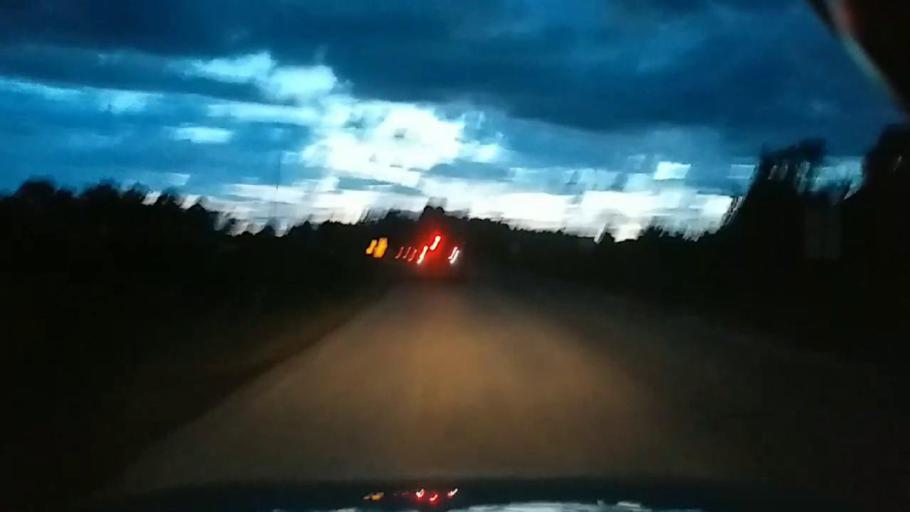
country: MY
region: Sarawak
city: Sibu
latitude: 2.4135
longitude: 112.1590
